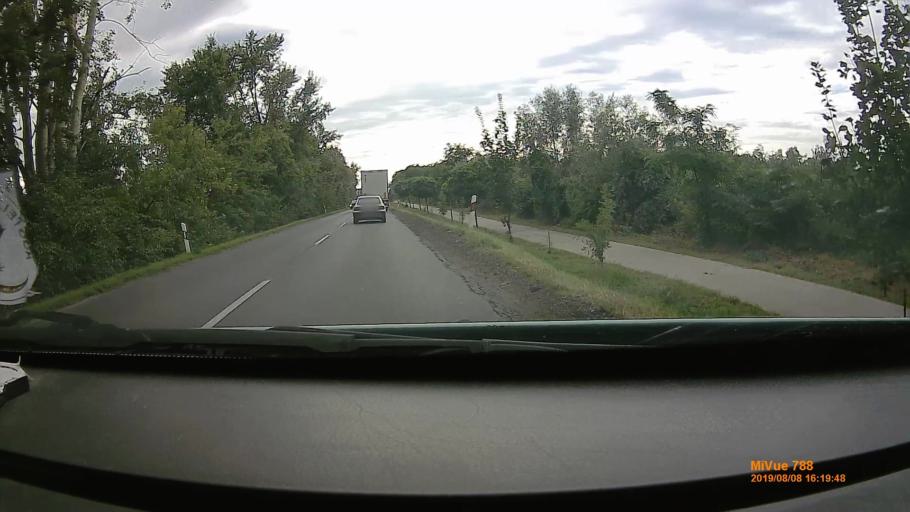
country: HU
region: Szabolcs-Szatmar-Bereg
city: Nyirmeggyes
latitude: 47.9664
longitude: 22.2726
